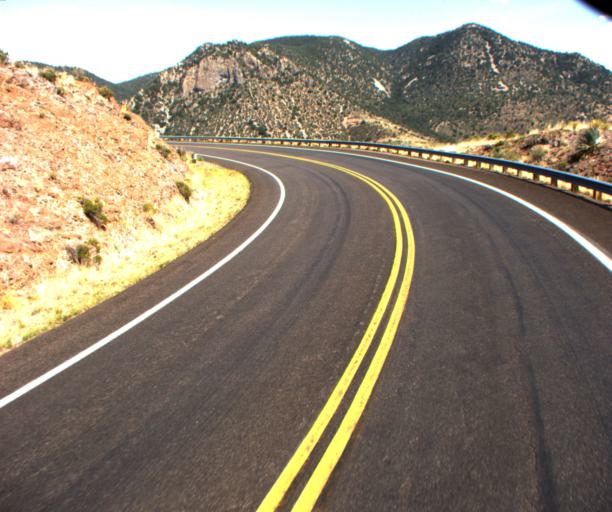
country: US
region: Arizona
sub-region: Greenlee County
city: Clifton
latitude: 33.0477
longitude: -109.1000
